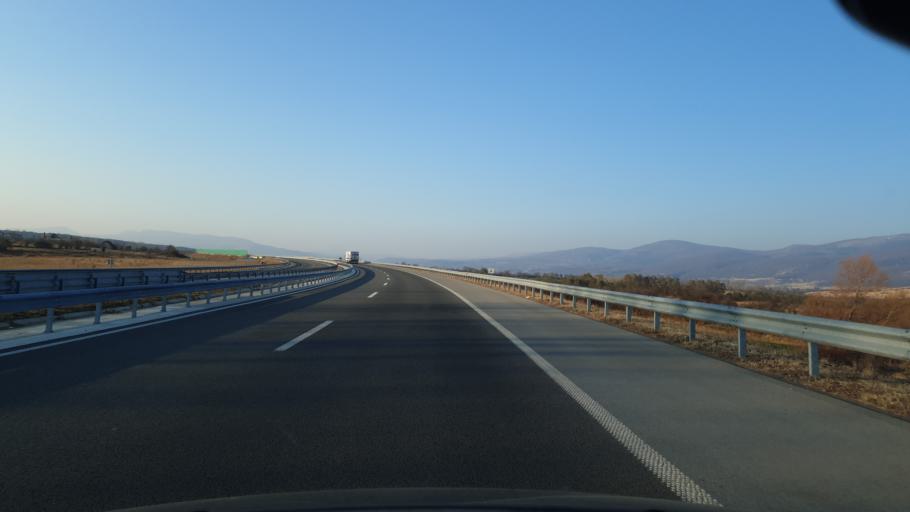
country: RS
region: Central Serbia
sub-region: Pirotski Okrug
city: Dimitrovgrad
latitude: 43.0689
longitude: 22.6780
